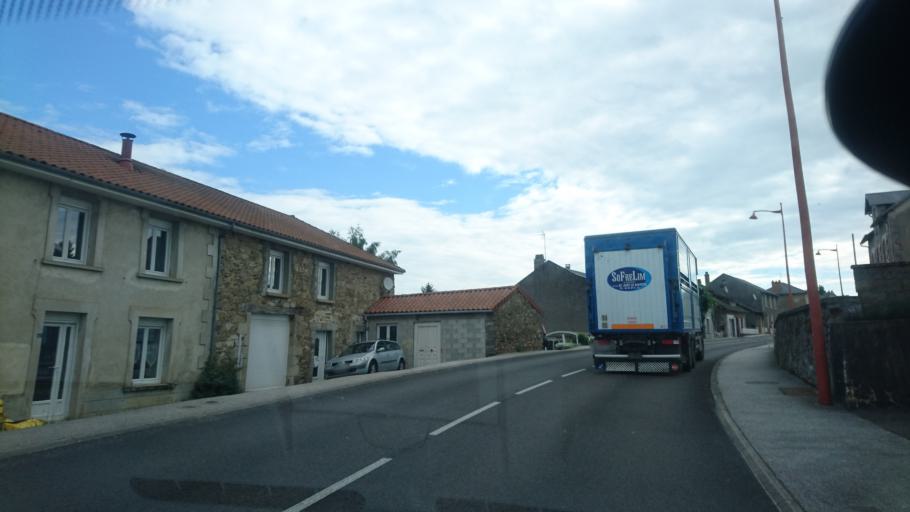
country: FR
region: Limousin
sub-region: Departement de la Haute-Vienne
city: Chateauneuf-la-Foret
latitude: 45.7107
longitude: 1.5993
